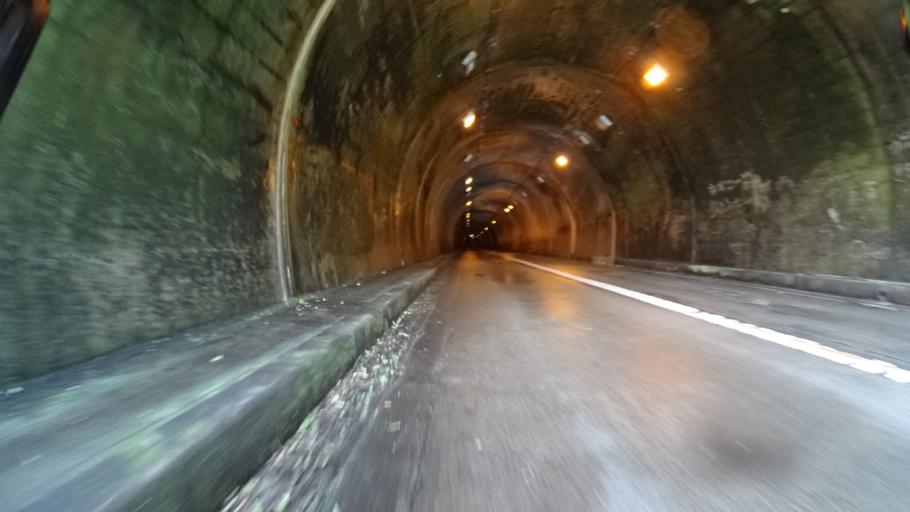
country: JP
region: Tokyo
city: Ome
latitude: 35.8423
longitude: 139.1963
